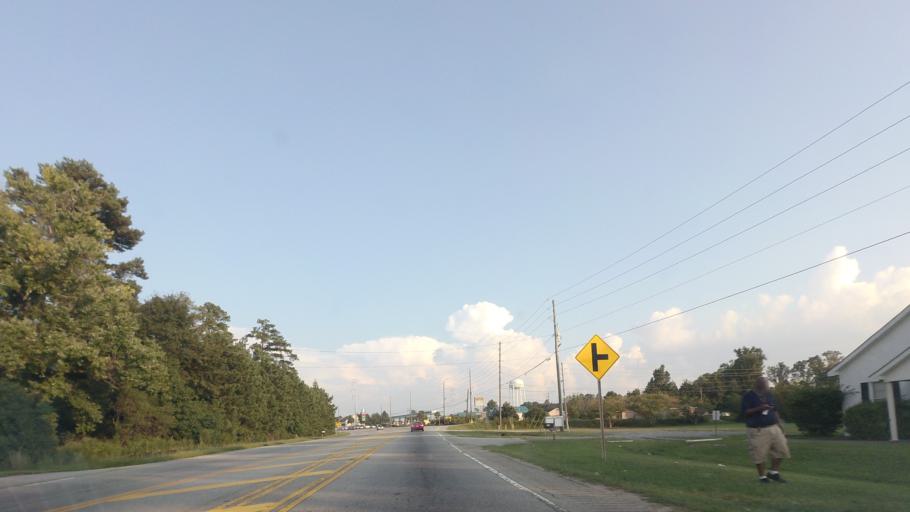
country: US
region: Georgia
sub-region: Bibb County
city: West Point
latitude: 32.8363
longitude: -83.7475
